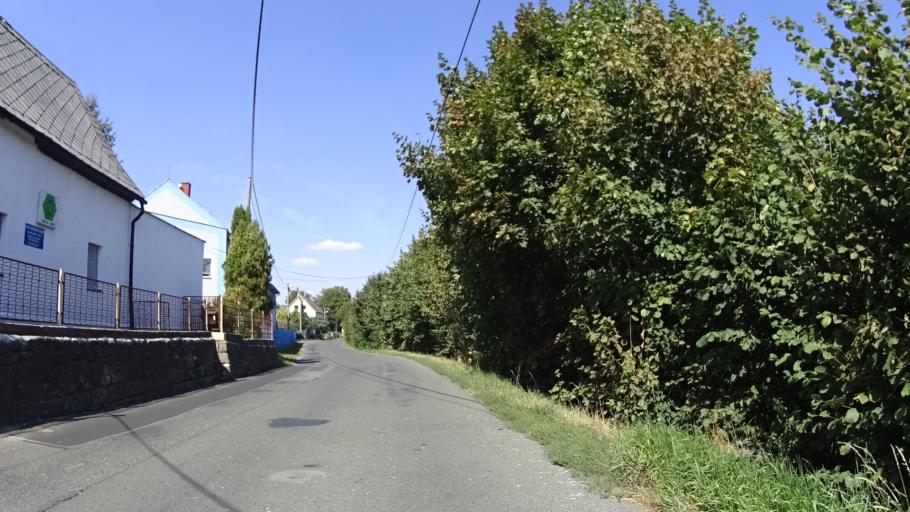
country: CZ
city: Hradek nad Nisou
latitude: 50.8378
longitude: 14.8625
